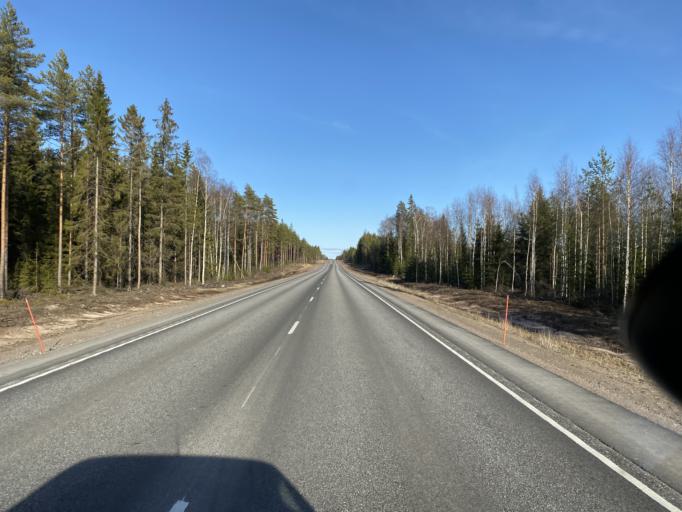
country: FI
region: Satakunta
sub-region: Rauma
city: Koeylioe
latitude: 61.1652
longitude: 22.3672
